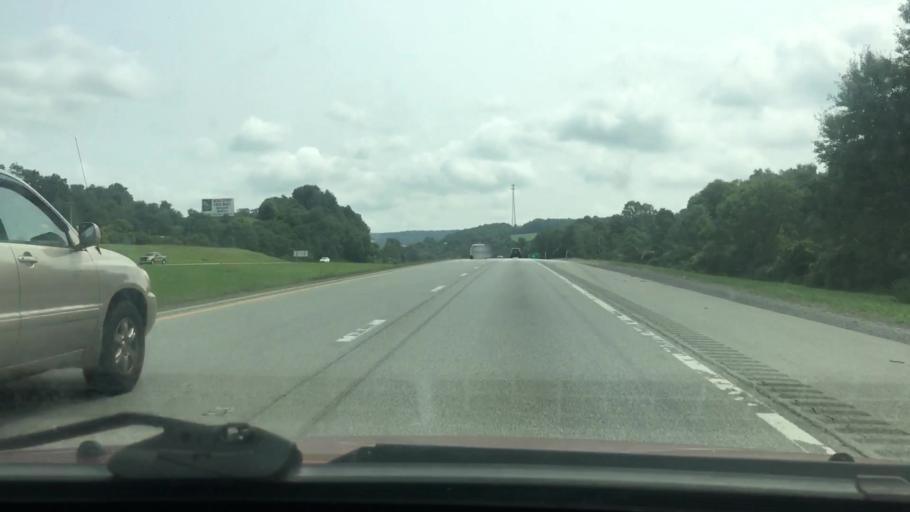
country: US
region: West Virginia
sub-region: Preston County
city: Terra Alta
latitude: 39.6566
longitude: -79.5513
